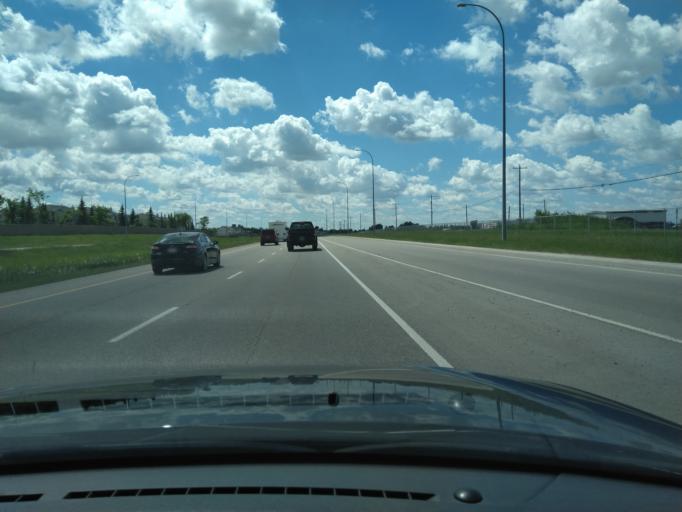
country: CA
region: Alberta
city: Calgary
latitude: 51.1239
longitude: -113.9703
